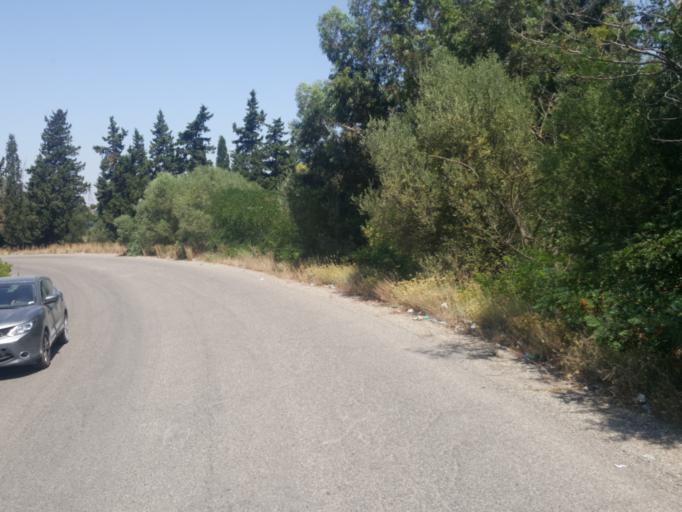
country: IT
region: Apulia
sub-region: Provincia di Taranto
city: Statte
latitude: 40.5063
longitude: 17.1936
